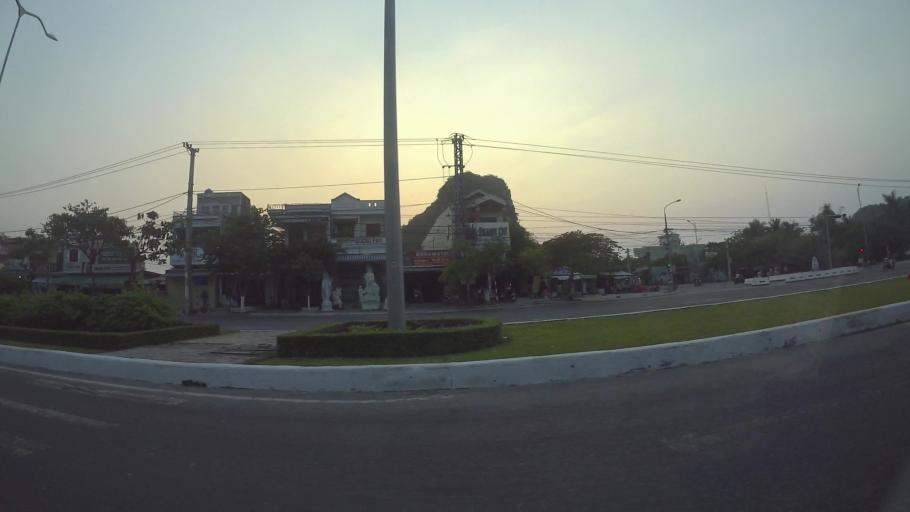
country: VN
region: Da Nang
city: Ngu Hanh Son
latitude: 16.0002
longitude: 108.2598
